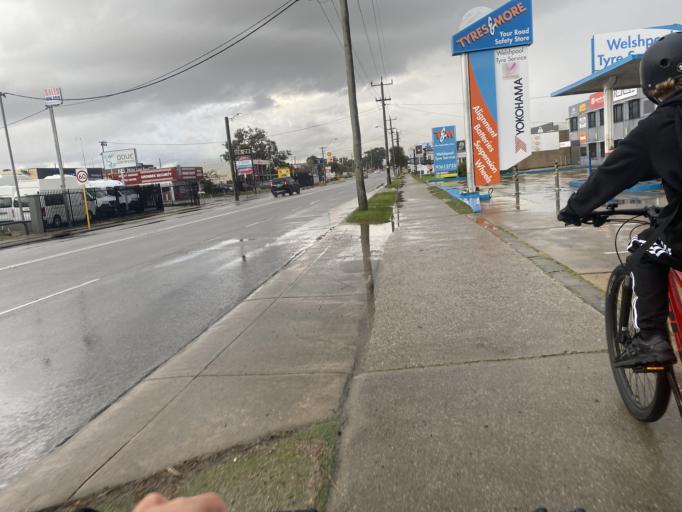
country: AU
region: Western Australia
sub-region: Canning
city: Bentley
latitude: -31.9940
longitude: 115.9174
